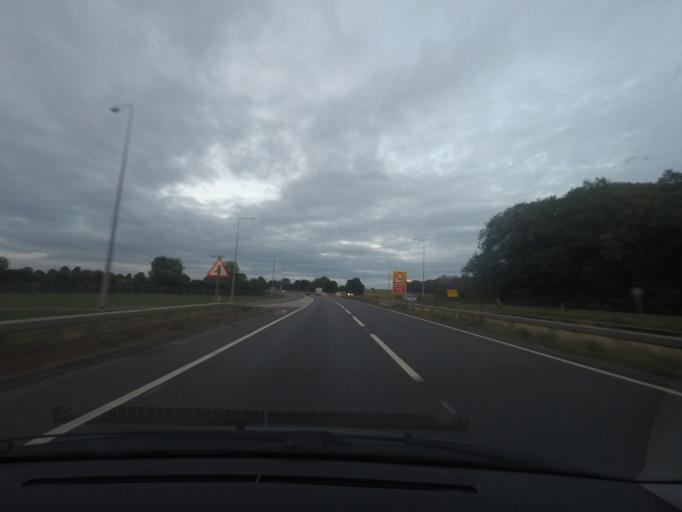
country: GB
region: England
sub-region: Northamptonshire
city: Irchester
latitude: 52.2882
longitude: -0.6609
